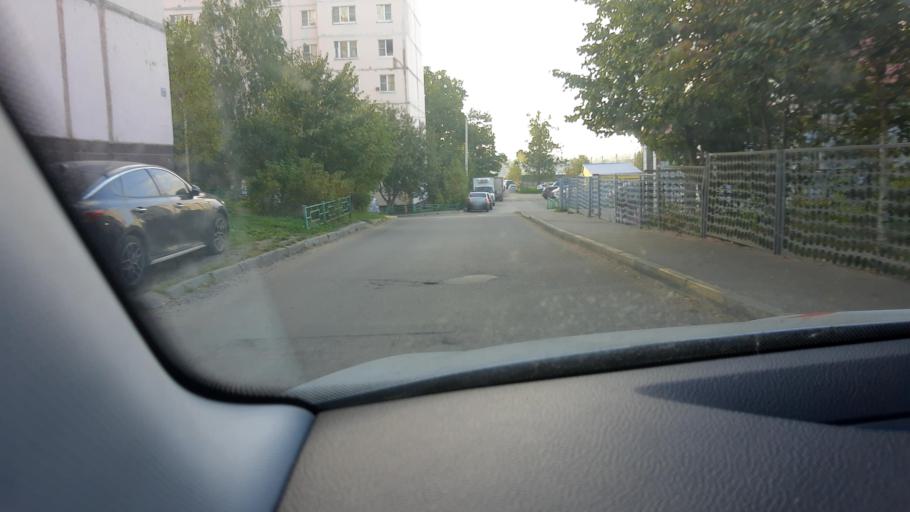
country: RU
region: Moskovskaya
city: Selyatino
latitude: 55.5526
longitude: 36.9716
